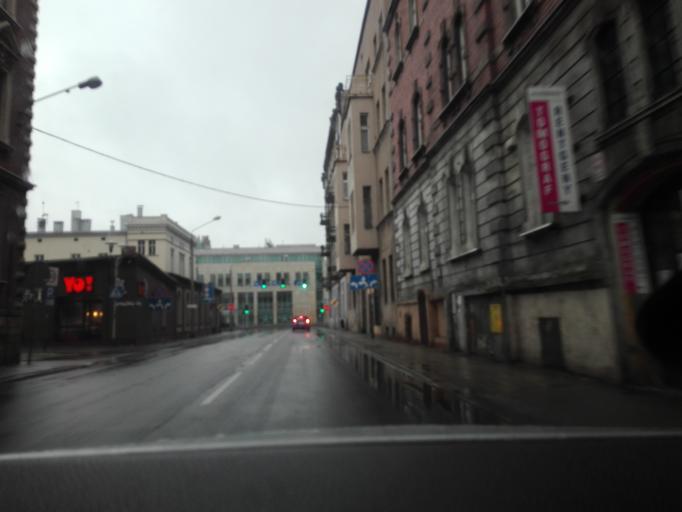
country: PL
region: Silesian Voivodeship
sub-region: Katowice
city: Katowice
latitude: 50.2575
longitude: 19.0281
